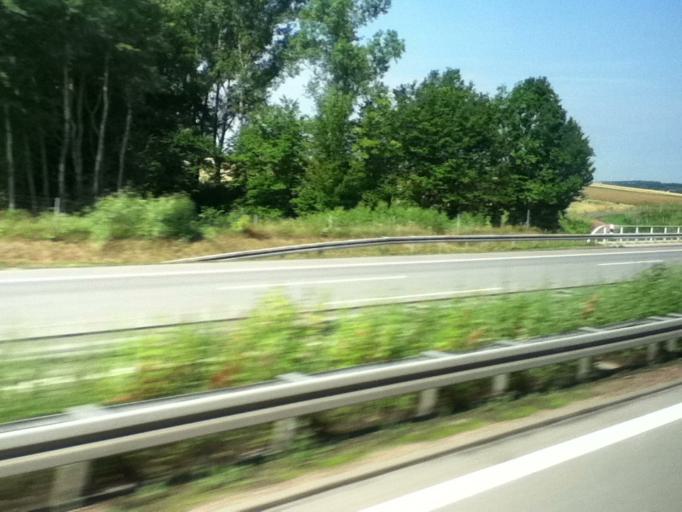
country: DE
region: Saxony
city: Remse
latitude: 50.8394
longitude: 12.5897
